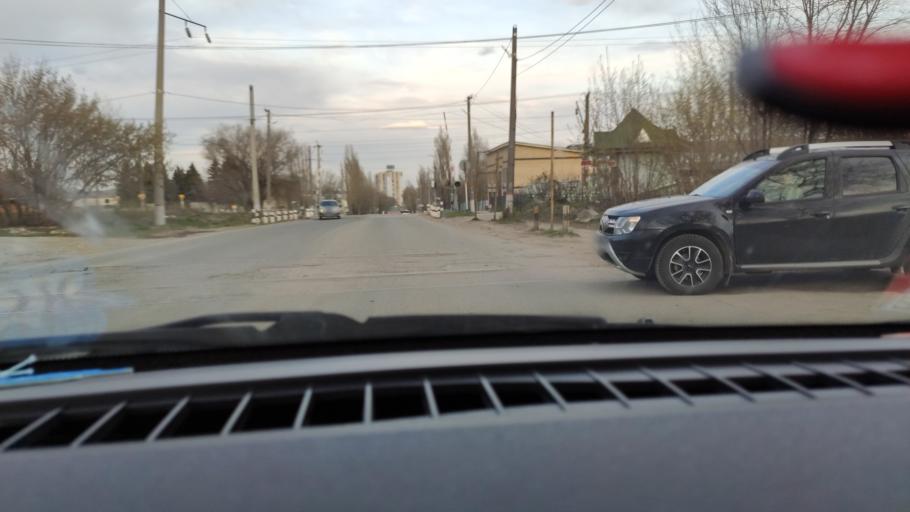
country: RU
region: Saratov
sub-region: Saratovskiy Rayon
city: Saratov
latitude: 51.6150
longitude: 45.9605
